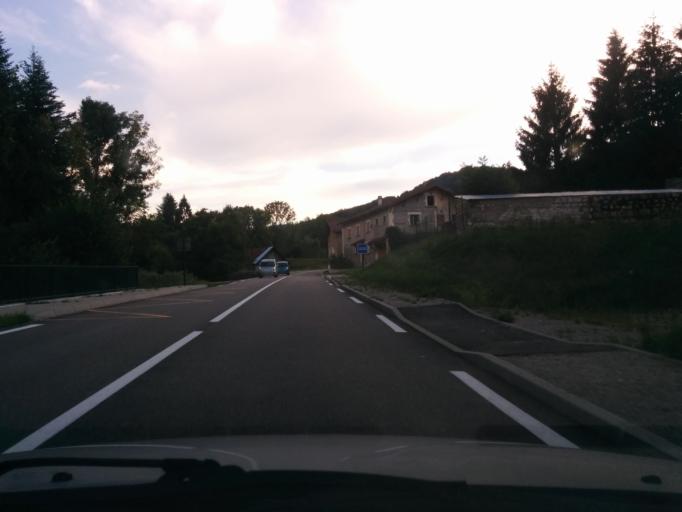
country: FR
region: Rhone-Alpes
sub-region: Departement de l'Isere
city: Saint-Aupre
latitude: 45.3517
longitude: 5.6714
